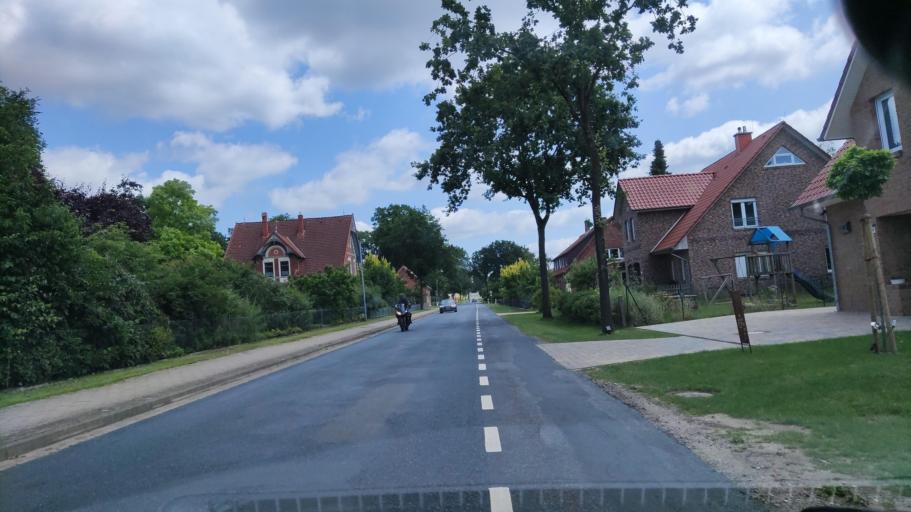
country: DE
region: Lower Saxony
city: Walsrode
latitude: 52.8302
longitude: 9.6444
